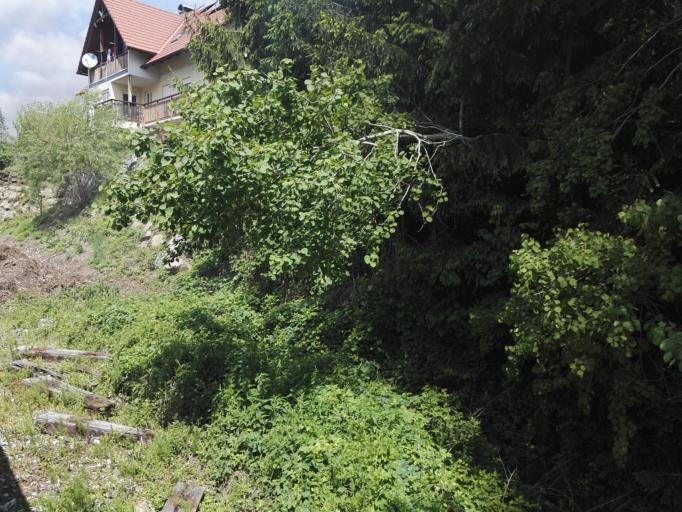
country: AT
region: Styria
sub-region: Politischer Bezirk Weiz
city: Anger
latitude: 47.2688
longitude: 15.7013
